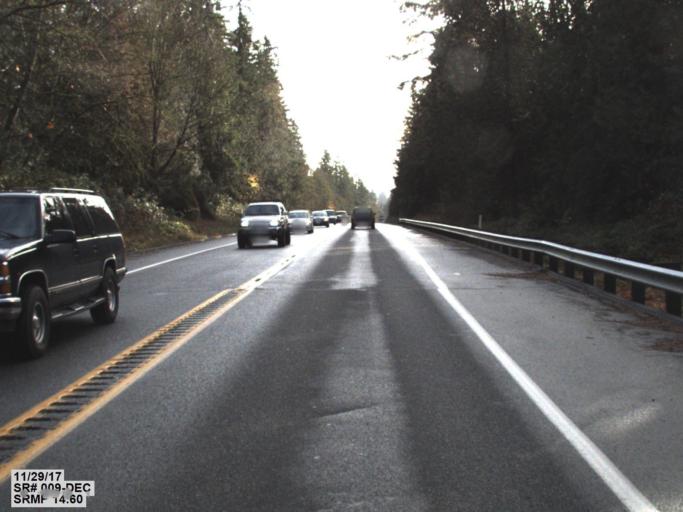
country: US
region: Washington
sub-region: Snohomish County
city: West Lake Stevens
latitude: 47.9862
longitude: -122.1035
